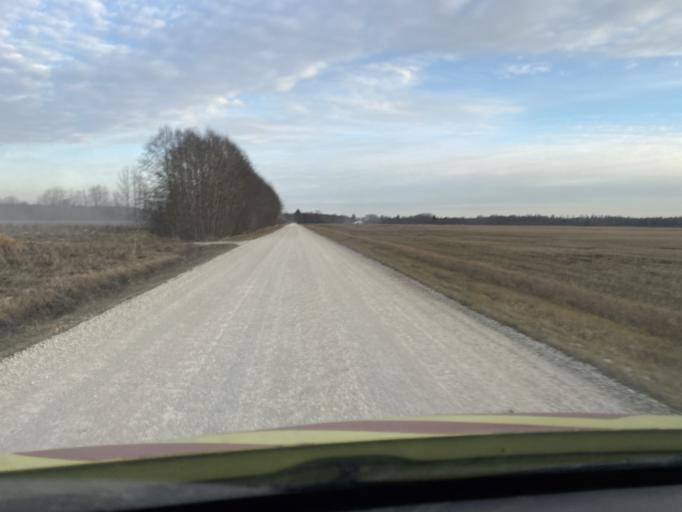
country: EE
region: Jogevamaa
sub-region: Poltsamaa linn
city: Poltsamaa
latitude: 58.5807
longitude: 26.1402
